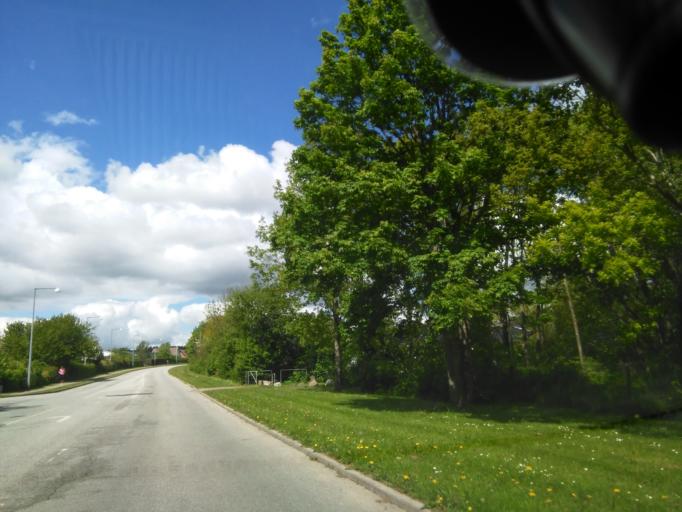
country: DK
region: Central Jutland
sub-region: Skanderborg Kommune
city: Horning
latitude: 56.0791
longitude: 10.0251
